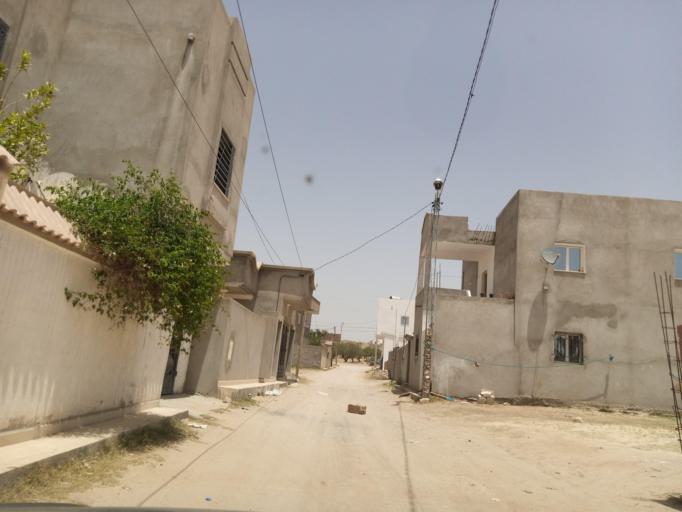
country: TN
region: Al Qasrayn
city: Kasserine
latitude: 35.2136
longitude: 8.8924
